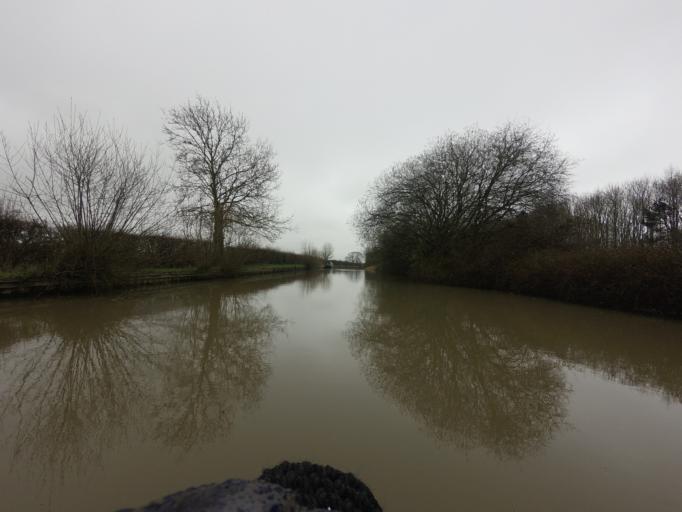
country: GB
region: England
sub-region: Milton Keynes
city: Castlethorpe
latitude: 52.0960
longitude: -0.8646
